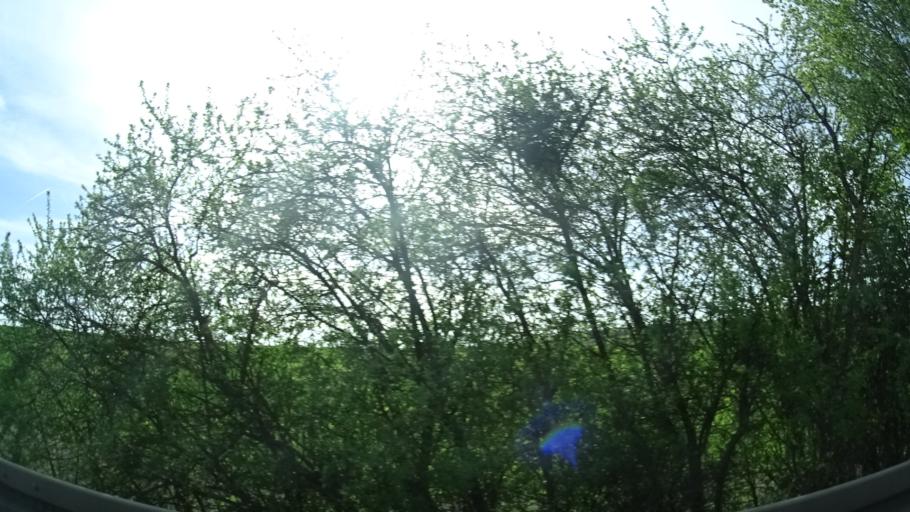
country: DE
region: Bavaria
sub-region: Regierungsbezirk Unterfranken
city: Volkach
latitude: 49.8850
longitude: 10.2280
